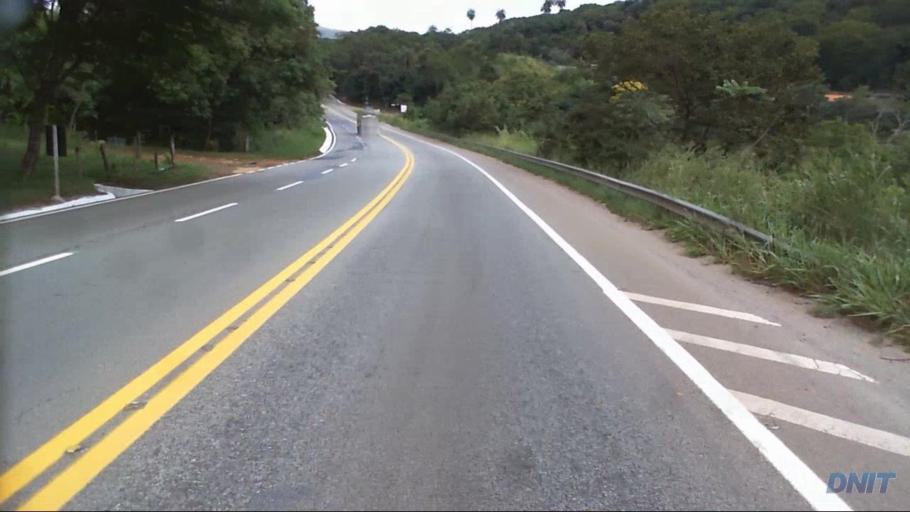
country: BR
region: Minas Gerais
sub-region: Santa Luzia
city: Santa Luzia
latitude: -19.7933
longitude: -43.7465
